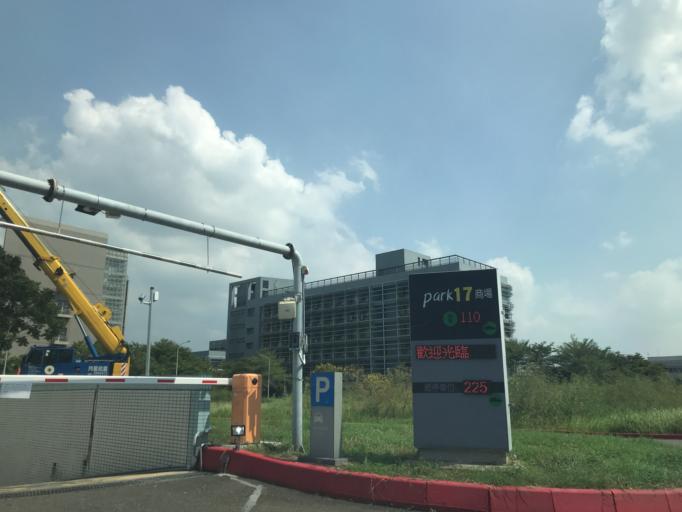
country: TW
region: Taiwan
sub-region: Tainan
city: Tainan
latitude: 23.0979
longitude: 120.2818
